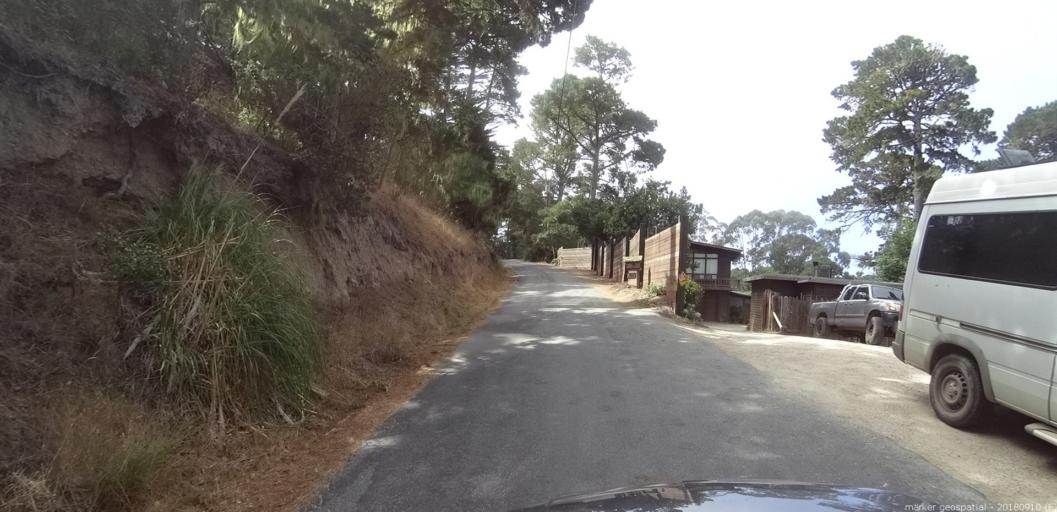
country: US
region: California
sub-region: Monterey County
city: Carmel-by-the-Sea
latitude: 36.5071
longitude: -121.9288
